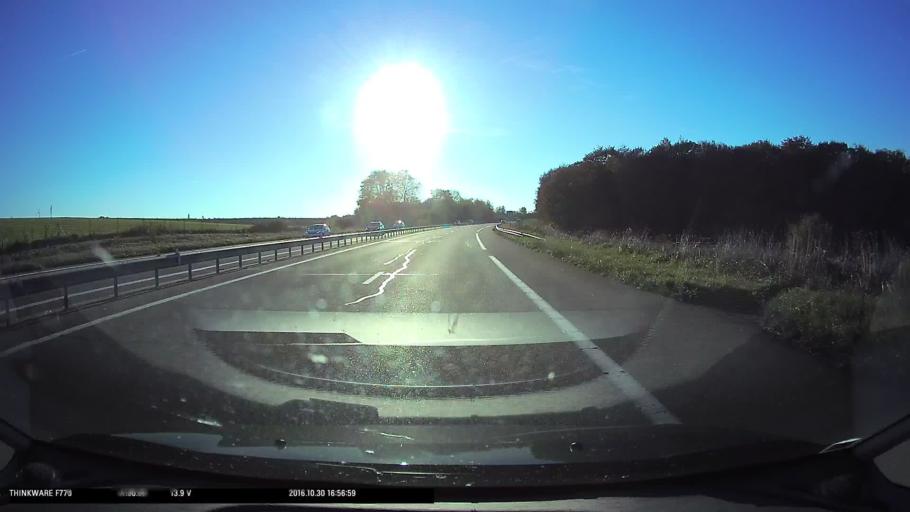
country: FR
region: Franche-Comte
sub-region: Departement du Doubs
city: Saint-Vit
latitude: 47.1943
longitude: 5.7983
